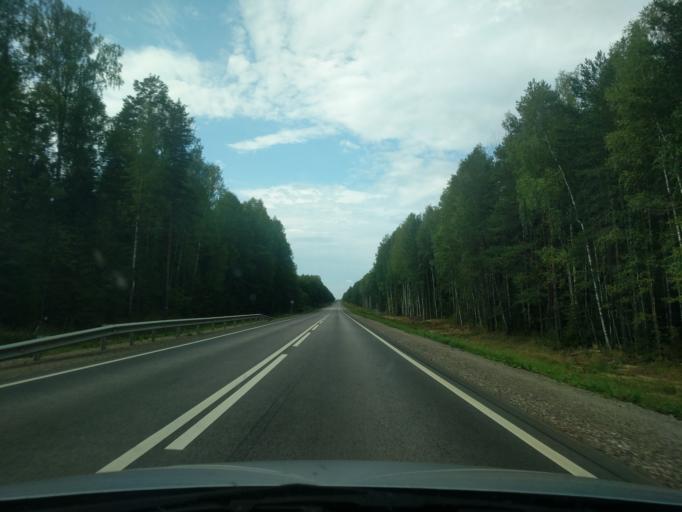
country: RU
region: Kostroma
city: Kadyy
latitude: 57.7953
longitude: 42.9385
